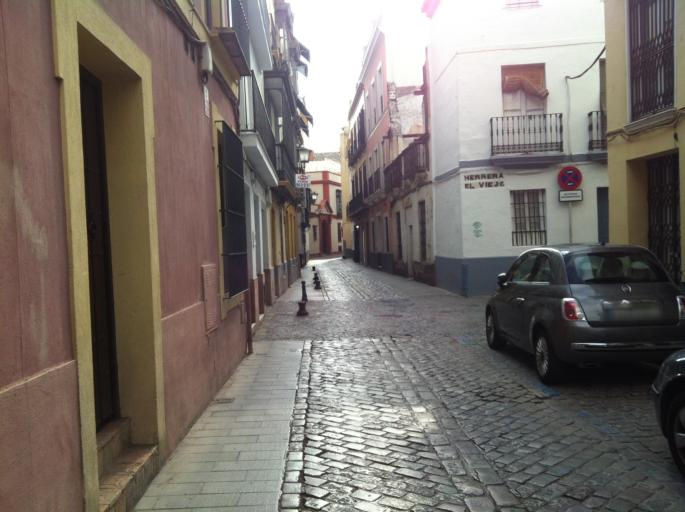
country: ES
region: Andalusia
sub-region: Provincia de Sevilla
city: Sevilla
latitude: 37.3923
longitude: -5.9993
